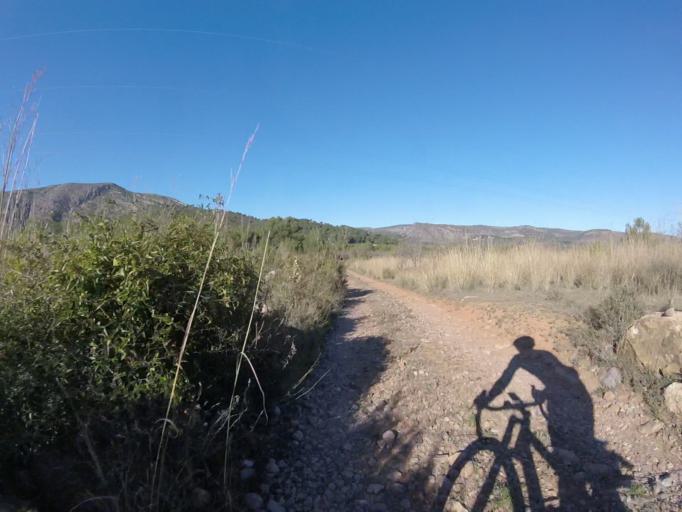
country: ES
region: Valencia
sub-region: Provincia de Castello
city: Orpesa/Oropesa del Mar
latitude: 40.1234
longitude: 0.1130
